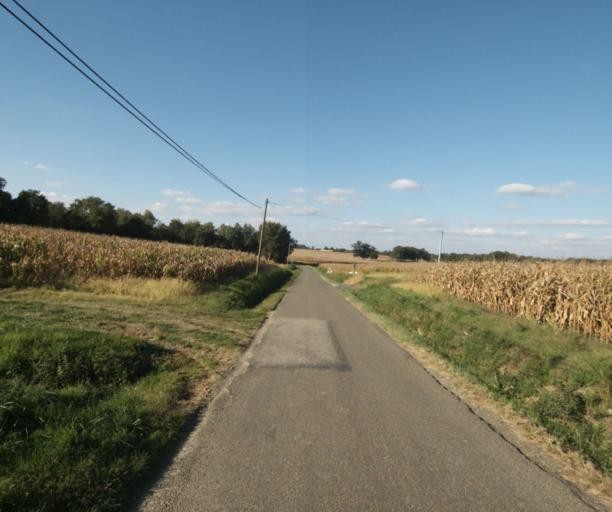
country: FR
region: Midi-Pyrenees
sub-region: Departement du Gers
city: Eauze
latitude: 43.8066
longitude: 0.1299
